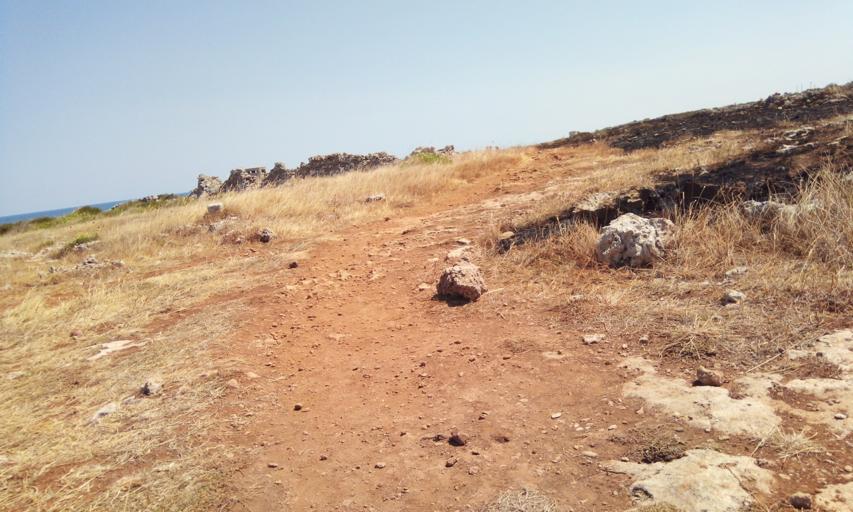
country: IT
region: Apulia
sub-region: Provincia di Bari
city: Polignano a Mare
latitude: 40.9846
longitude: 17.2486
